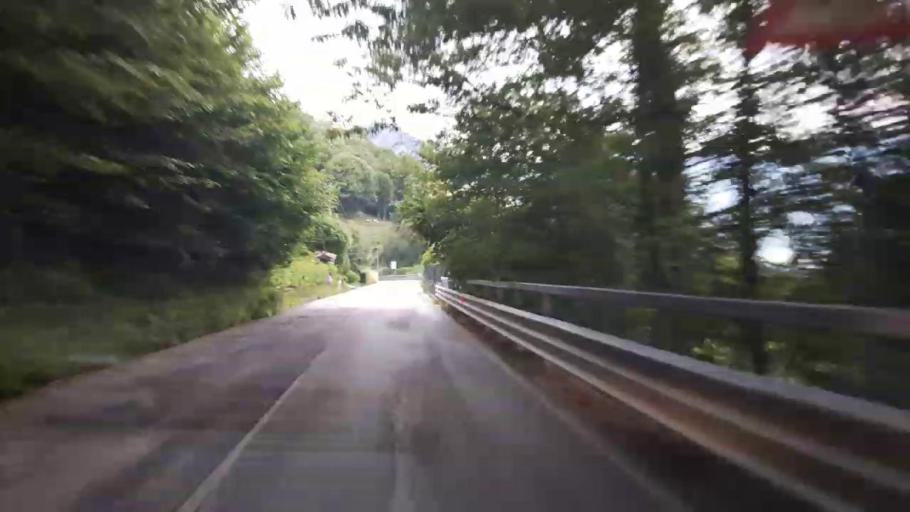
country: IT
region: Piedmont
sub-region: Provincia Verbano-Cusio-Ossola
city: Baveno
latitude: 45.8916
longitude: 8.5092
